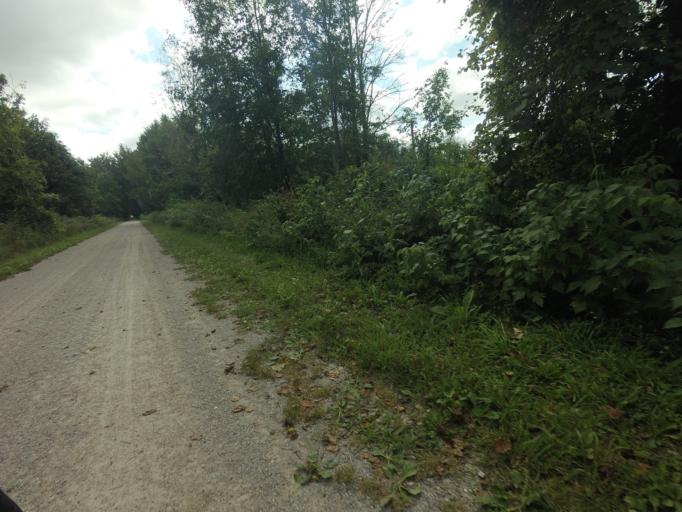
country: CA
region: Ontario
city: Huron East
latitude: 43.6143
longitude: -81.1398
